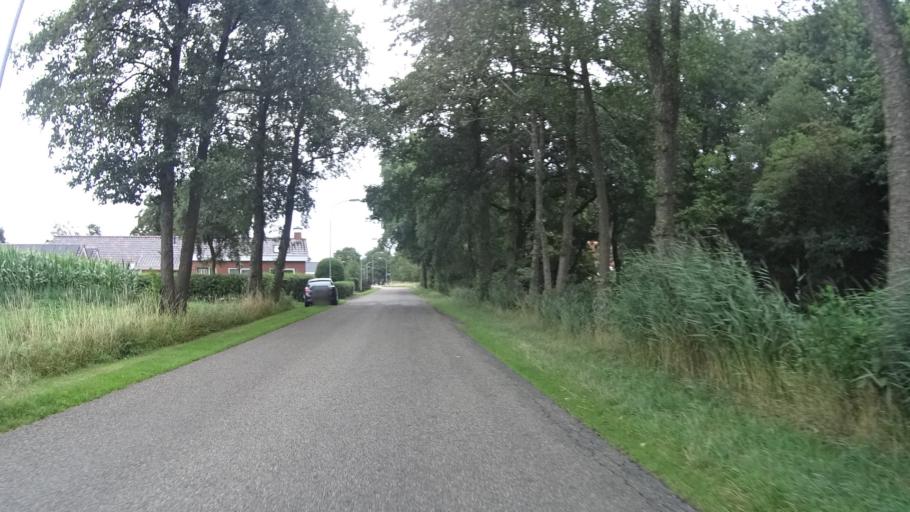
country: NL
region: Groningen
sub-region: Gemeente Slochteren
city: Slochteren
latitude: 53.2244
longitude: 6.7963
